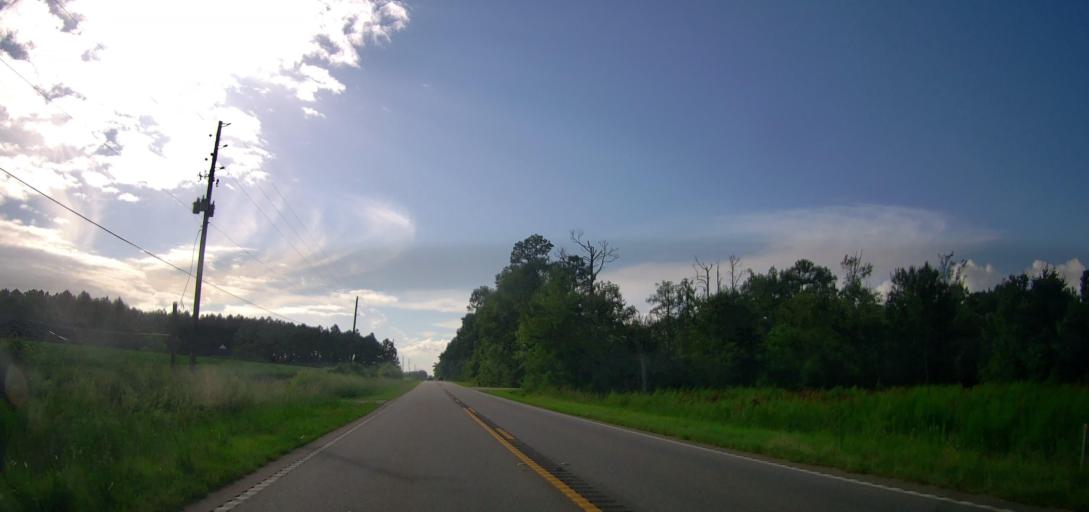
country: US
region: Georgia
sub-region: Coffee County
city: Douglas
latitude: 31.4785
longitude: -82.7897
